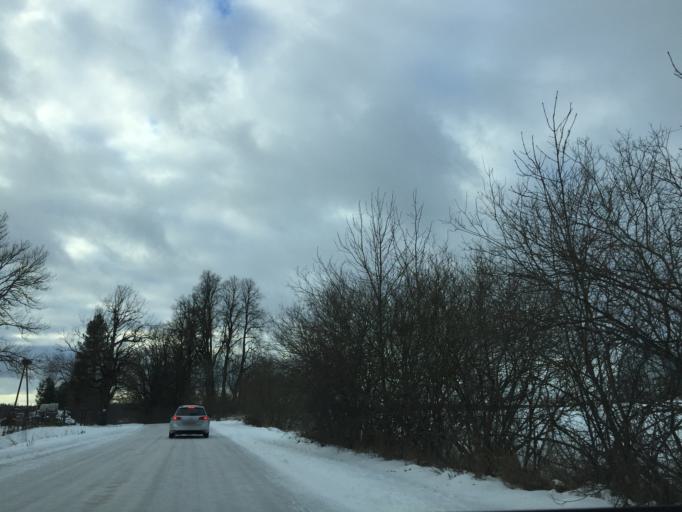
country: LV
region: Lielvarde
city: Lielvarde
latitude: 56.6111
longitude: 24.7633
